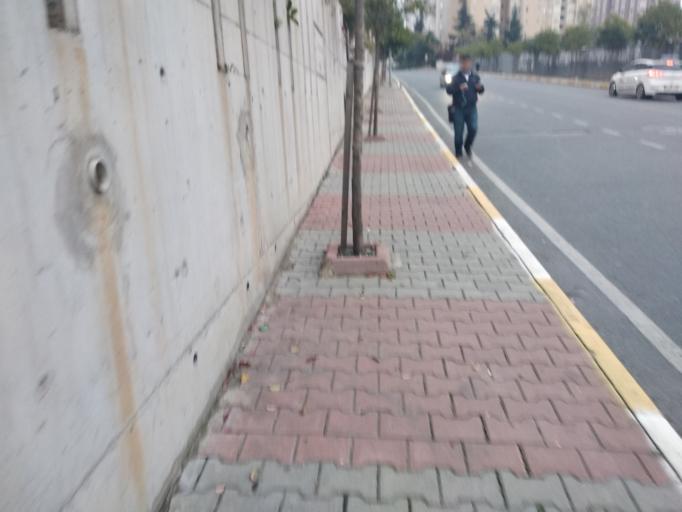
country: TR
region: Istanbul
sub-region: Atasehir
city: Atasehir
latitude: 40.9844
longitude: 29.1210
